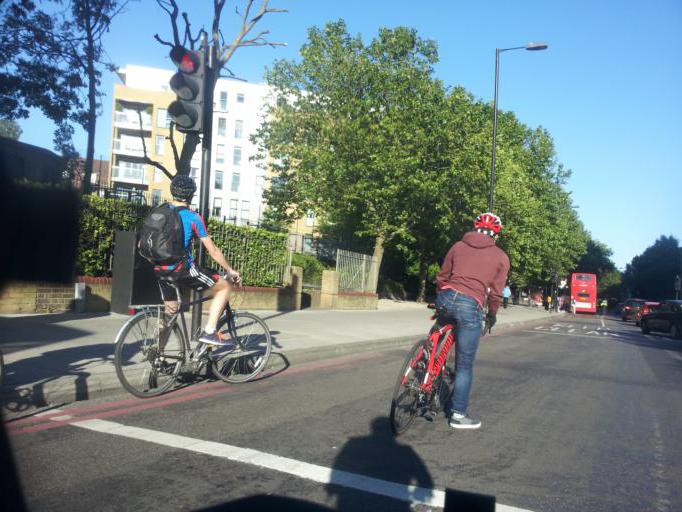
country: GB
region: England
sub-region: Greater London
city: City of London
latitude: 51.4988
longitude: -0.0705
